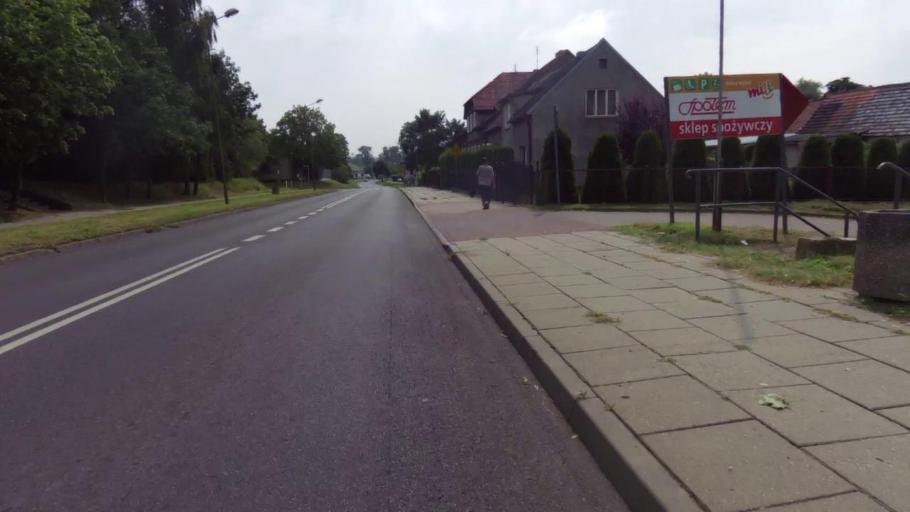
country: PL
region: West Pomeranian Voivodeship
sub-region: Powiat choszczenski
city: Choszczno
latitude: 53.1756
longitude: 15.4130
